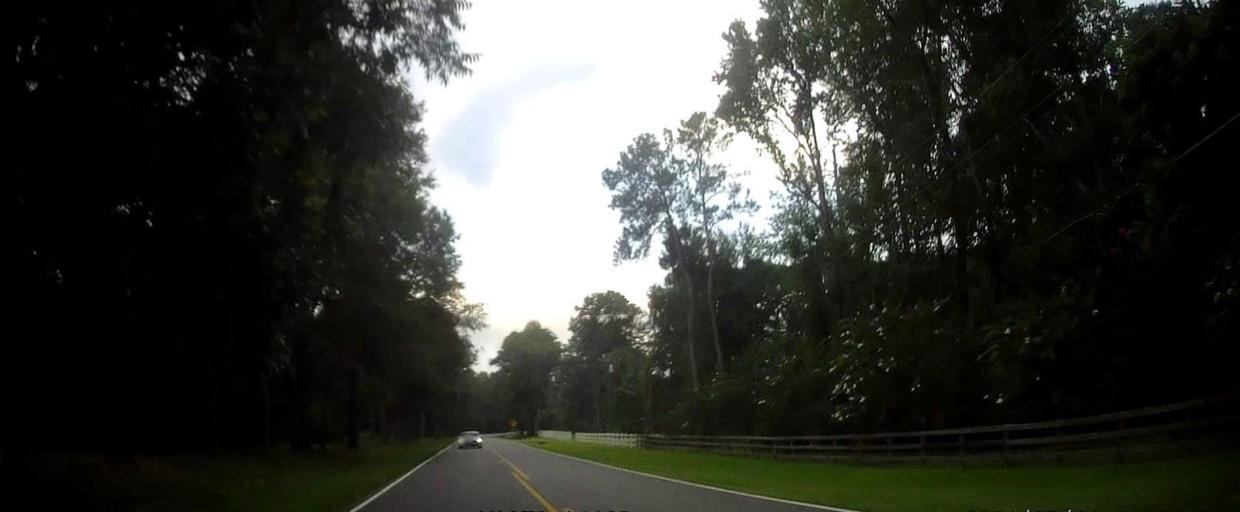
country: US
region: Georgia
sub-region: Laurens County
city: Dublin
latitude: 32.5819
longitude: -82.9033
